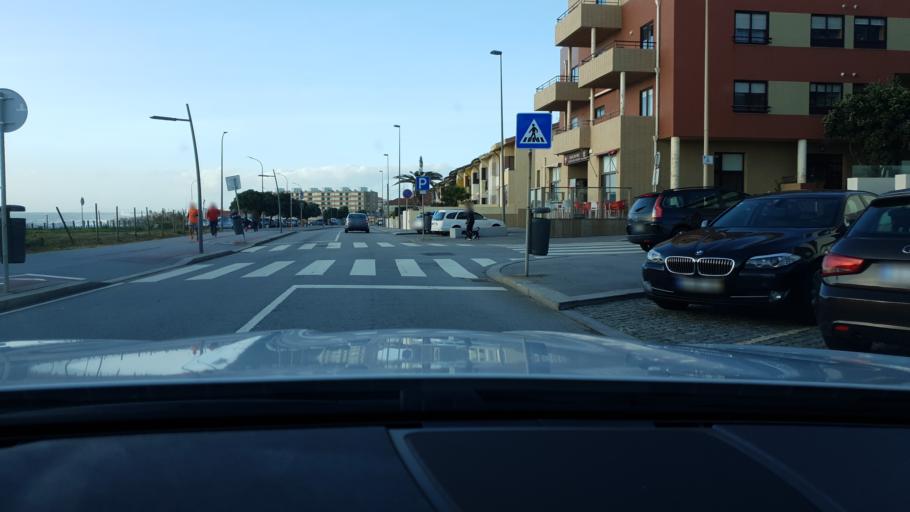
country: PT
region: Porto
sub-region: Matosinhos
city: Santa Cruz do Bispo
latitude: 41.2232
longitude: -8.7151
